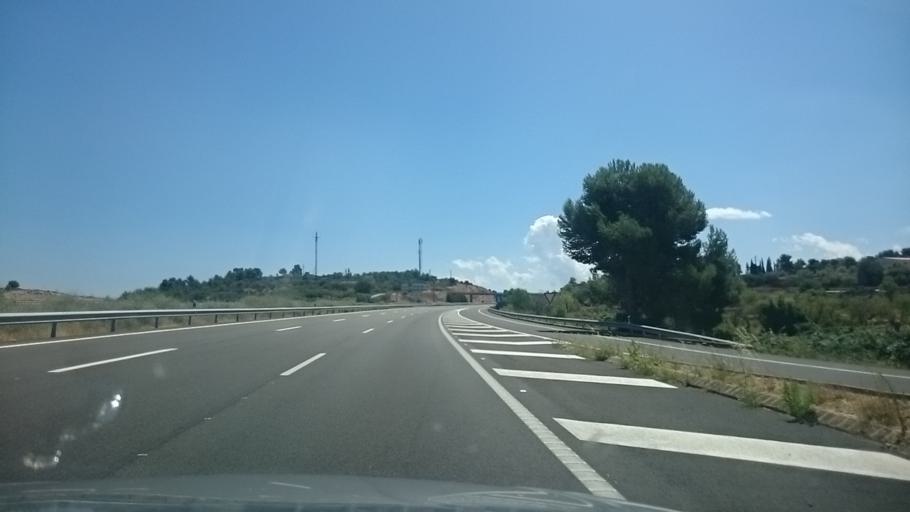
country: ES
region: Catalonia
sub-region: Provincia de Lleida
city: Vinaixa
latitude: 41.4288
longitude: 0.9389
